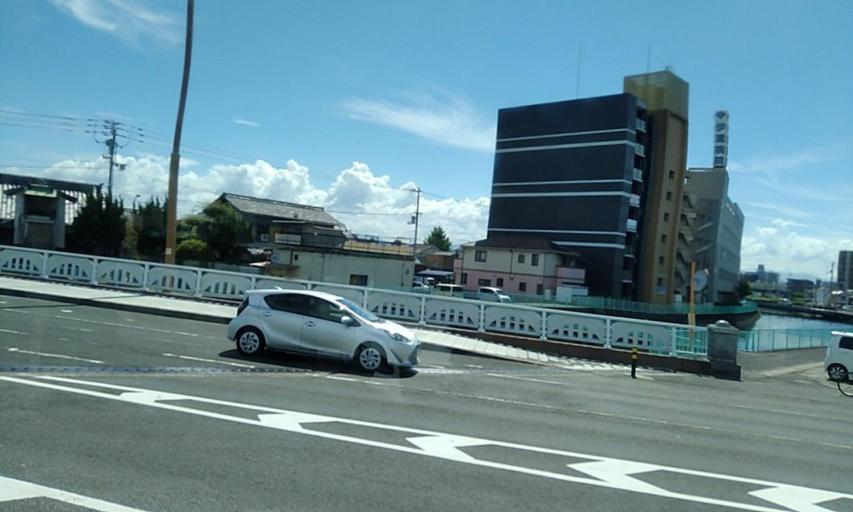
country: JP
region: Kagawa
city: Takamatsu-shi
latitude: 34.3350
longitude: 134.0613
